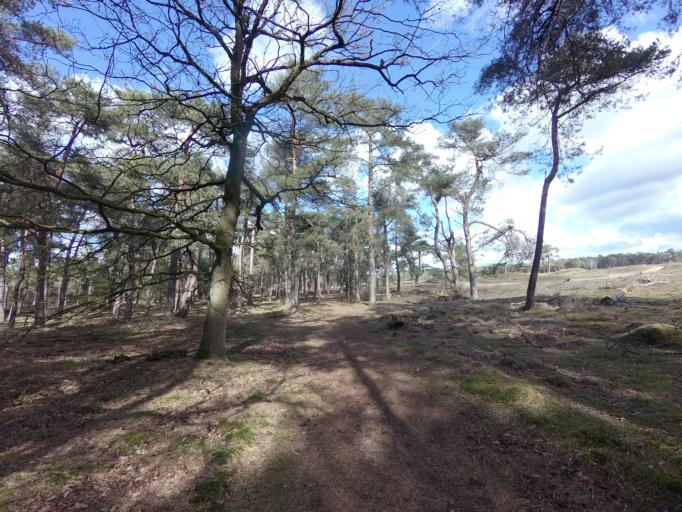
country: NL
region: Utrecht
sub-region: Gemeente Utrechtse Heuvelrug
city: Driebergen-Rijsenburg
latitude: 52.0738
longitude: 5.2809
